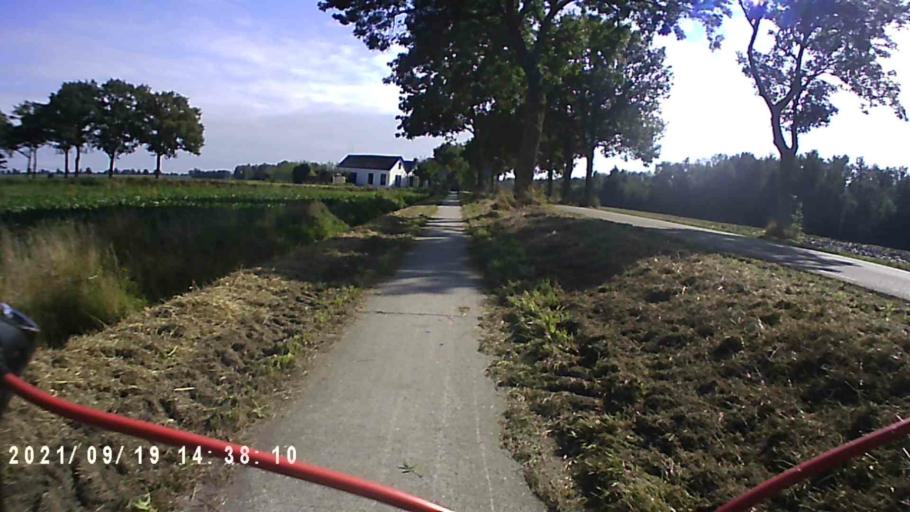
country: DE
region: Lower Saxony
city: Bunde
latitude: 53.1324
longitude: 7.1620
